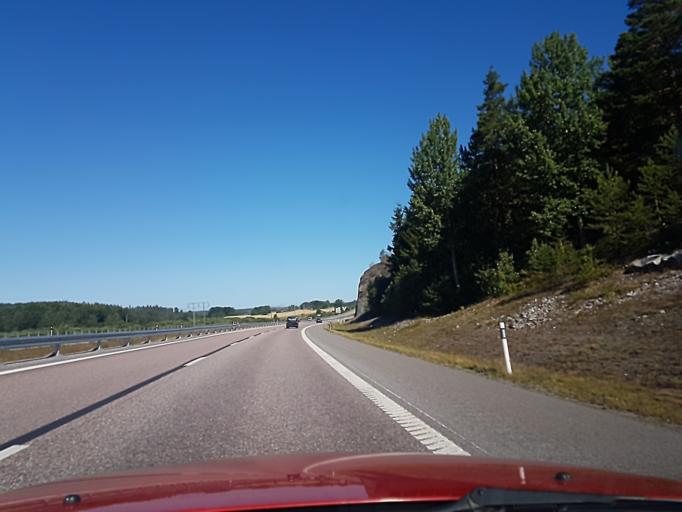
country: SE
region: Soedermanland
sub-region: Strangnas Kommun
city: Mariefred
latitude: 59.2524
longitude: 17.1535
